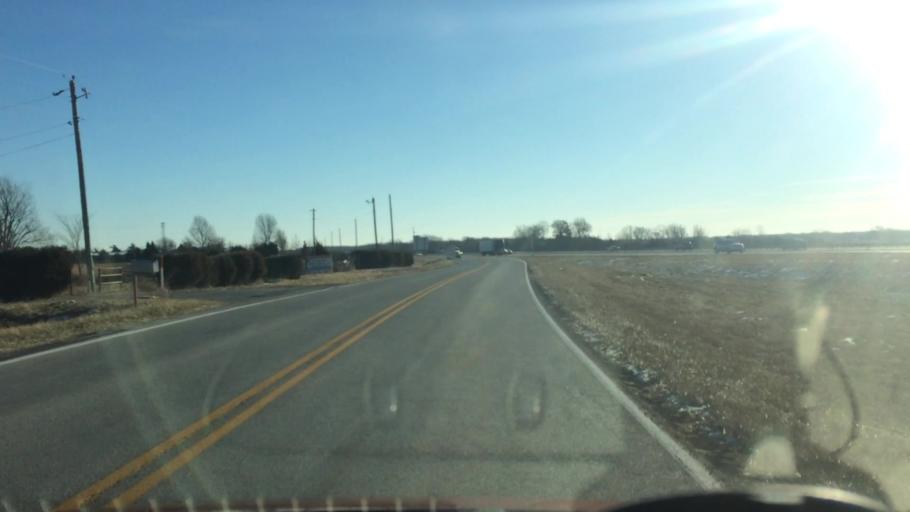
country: US
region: Missouri
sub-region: Greene County
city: Strafford
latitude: 37.2714
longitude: -93.1001
